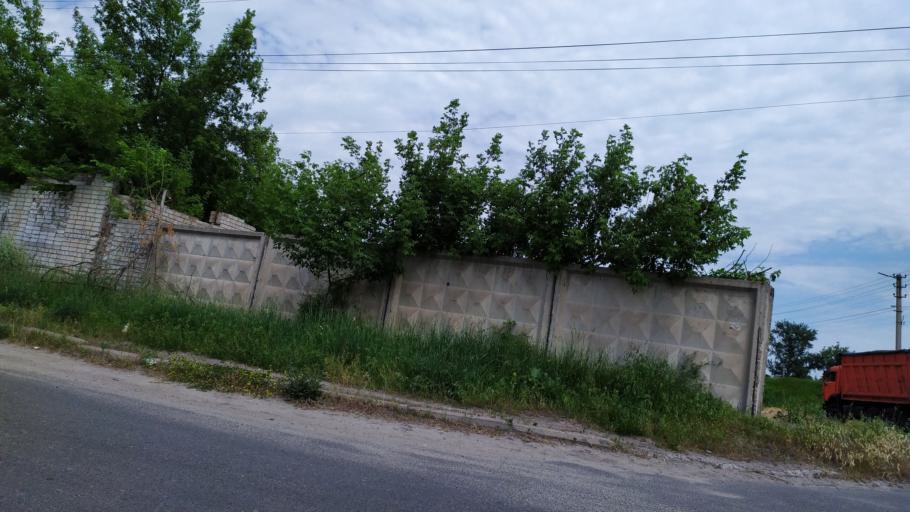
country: RU
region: Kursk
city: Kursk
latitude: 51.6604
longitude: 36.1533
